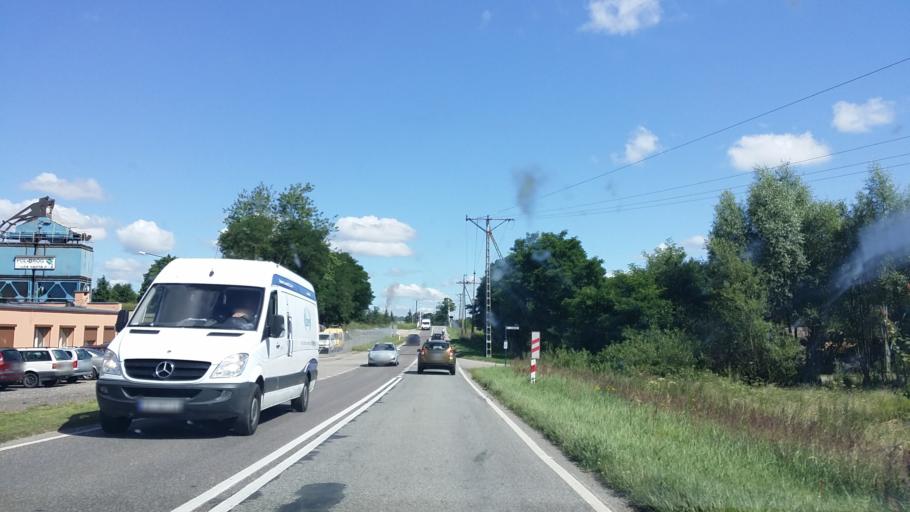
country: PL
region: West Pomeranian Voivodeship
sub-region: Powiat drawski
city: Drawsko Pomorskie
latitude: 53.5161
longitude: 15.7861
